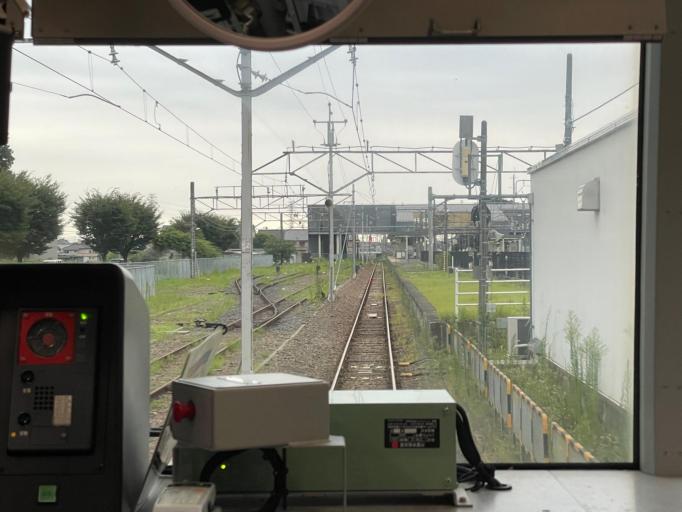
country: JP
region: Tochigi
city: Ujiie
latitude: 36.6334
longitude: 139.9792
